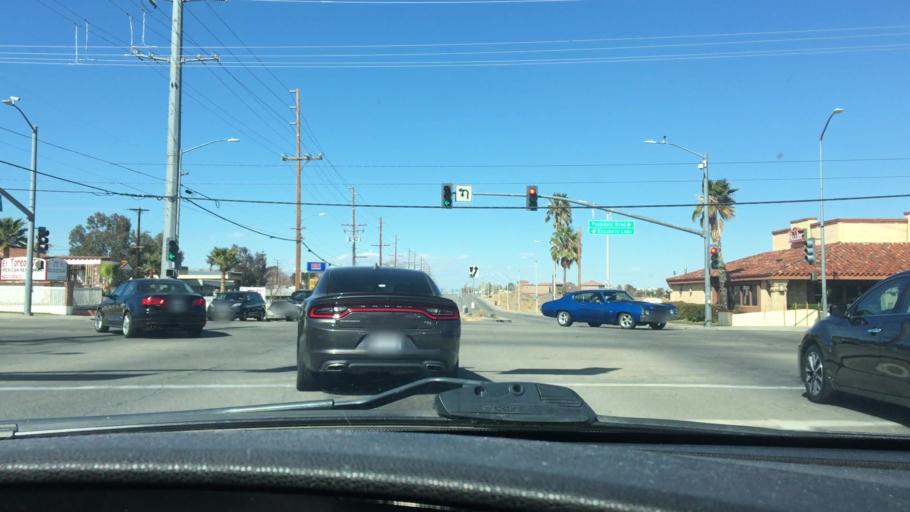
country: US
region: California
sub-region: Los Angeles County
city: Desert View Highlands
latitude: 34.5869
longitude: -118.1474
